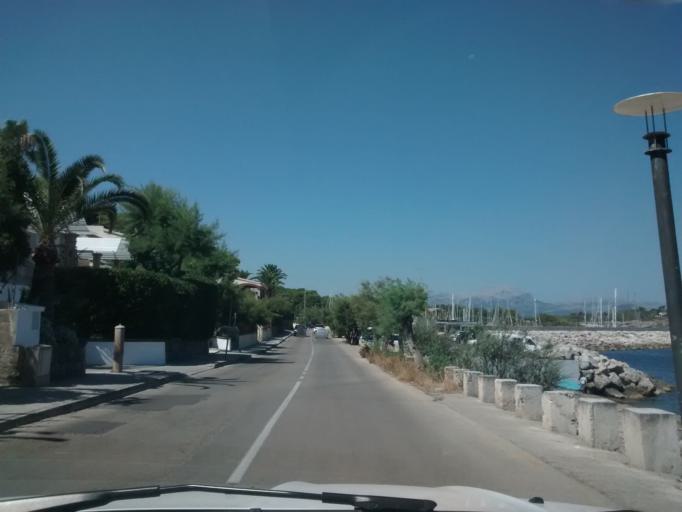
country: ES
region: Balearic Islands
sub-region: Illes Balears
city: Port d'Alcudia
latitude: 39.8665
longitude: 3.1476
